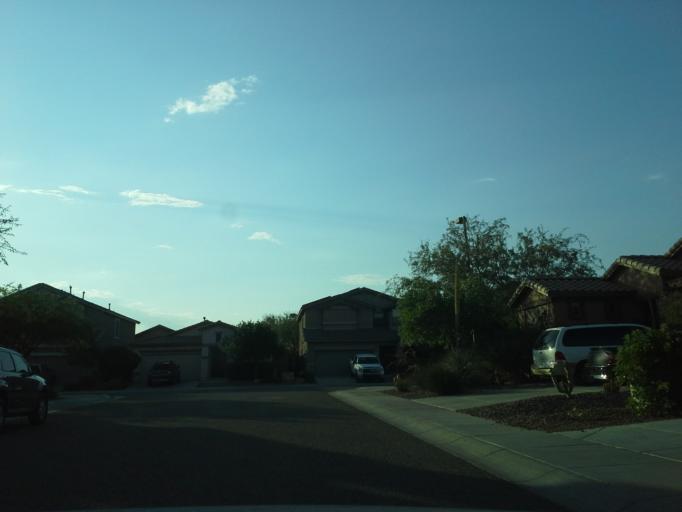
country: US
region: Arizona
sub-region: Maricopa County
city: Anthem
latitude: 33.8655
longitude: -112.1552
